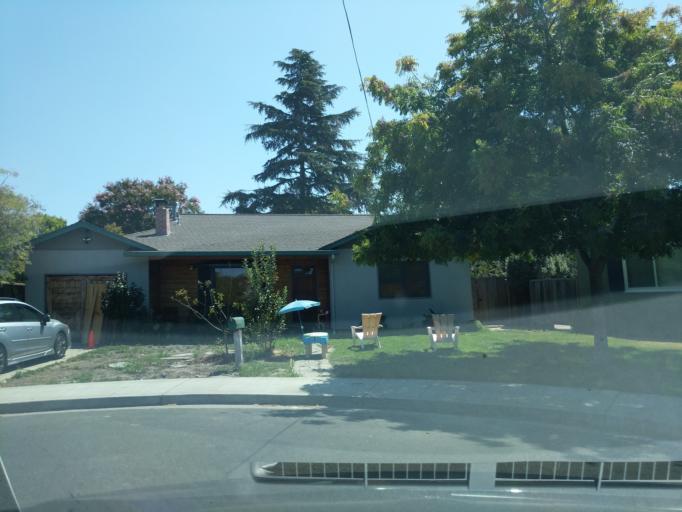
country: US
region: California
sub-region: Santa Clara County
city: Mountain View
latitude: 37.3859
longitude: -122.0744
